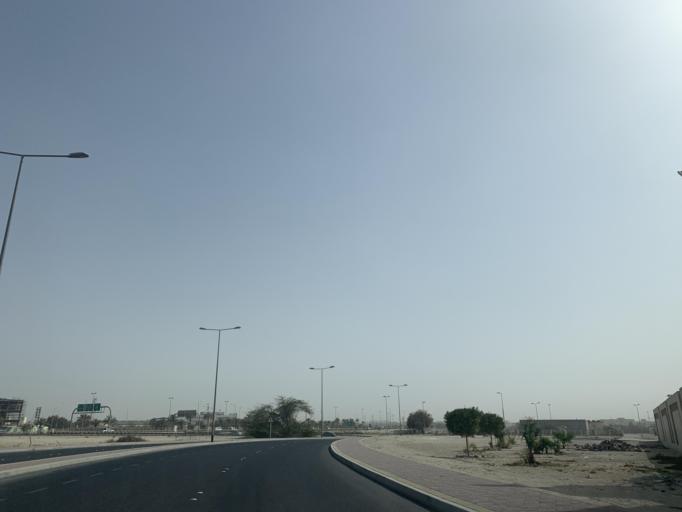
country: BH
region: Northern
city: Madinat `Isa
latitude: 26.1630
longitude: 50.5391
